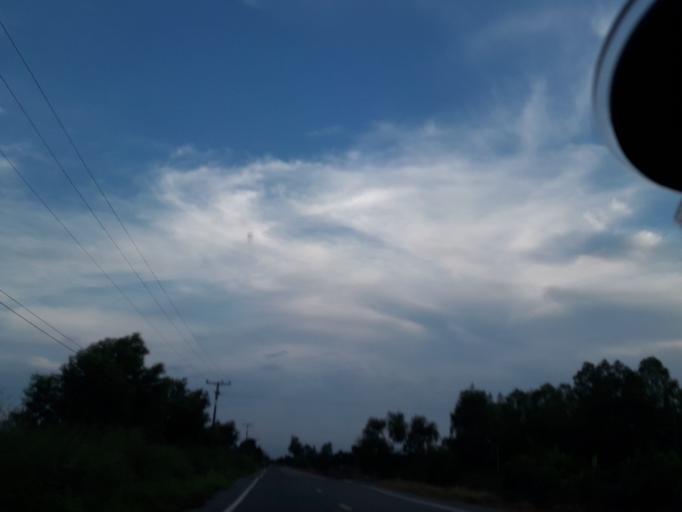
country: TH
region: Sara Buri
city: Nong Khae
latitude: 14.2538
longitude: 100.8688
